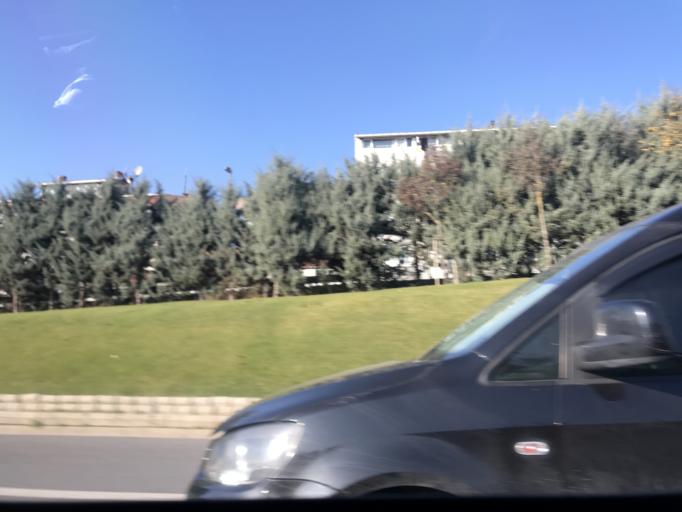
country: TR
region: Istanbul
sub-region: Atasehir
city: Atasehir
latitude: 41.0076
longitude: 29.0796
